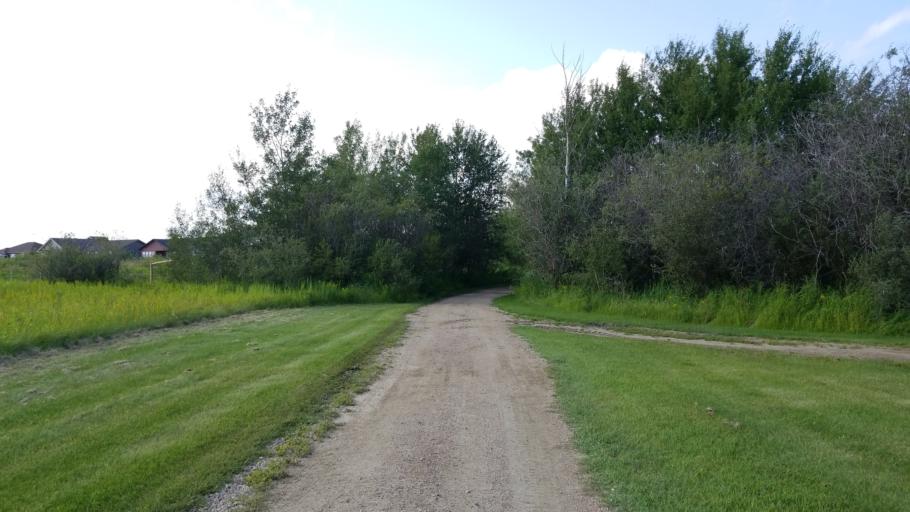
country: CA
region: Saskatchewan
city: Lloydminster
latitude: 53.2595
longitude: -110.0476
